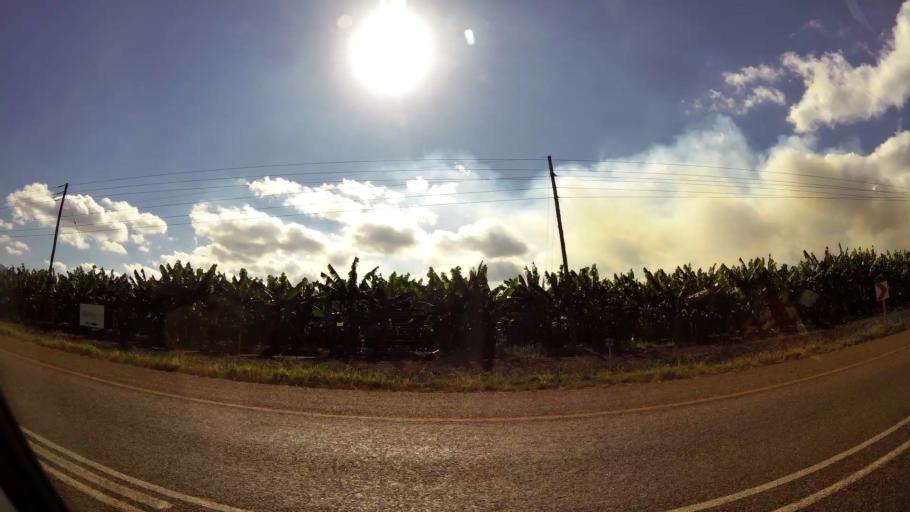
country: ZA
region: Limpopo
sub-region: Mopani District Municipality
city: Tzaneen
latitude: -23.8032
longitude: 30.1162
